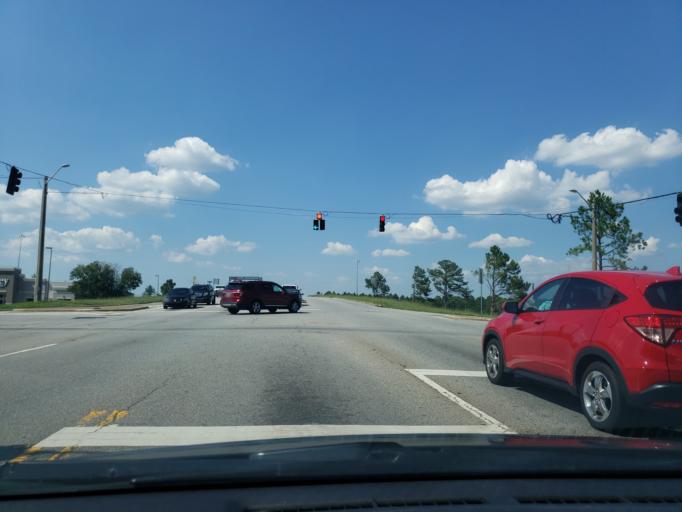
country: US
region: Georgia
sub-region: Dougherty County
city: Albany
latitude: 31.6152
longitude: -84.2042
